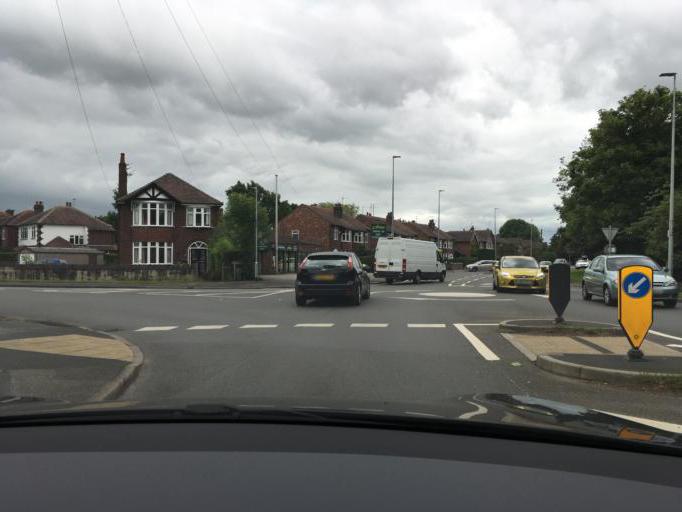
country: GB
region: England
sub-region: Cheshire East
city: Poynton
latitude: 53.3459
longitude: -2.1238
